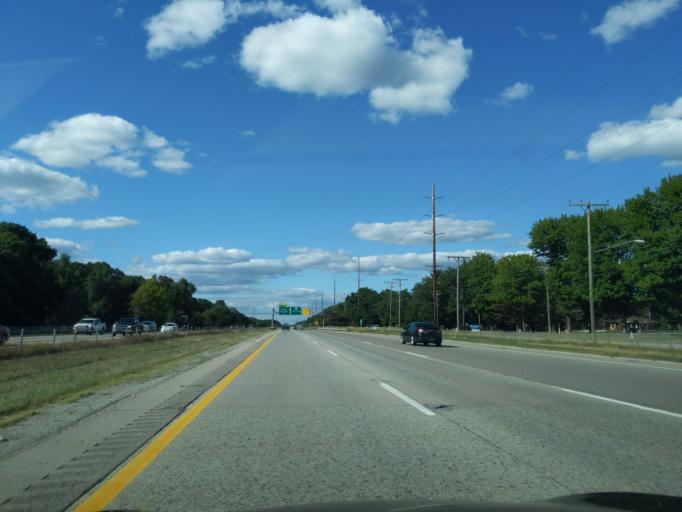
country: US
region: Michigan
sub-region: Muskegon County
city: Muskegon
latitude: 43.2381
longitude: -86.2045
